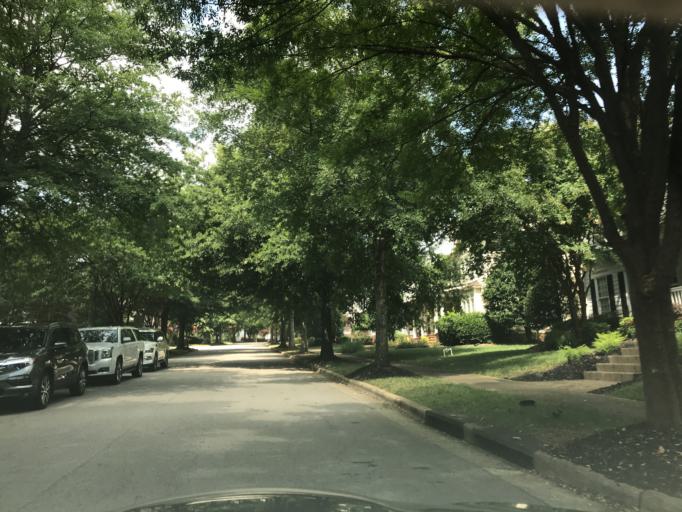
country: US
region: North Carolina
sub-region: Wake County
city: Wake Forest
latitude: 35.9264
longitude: -78.5680
